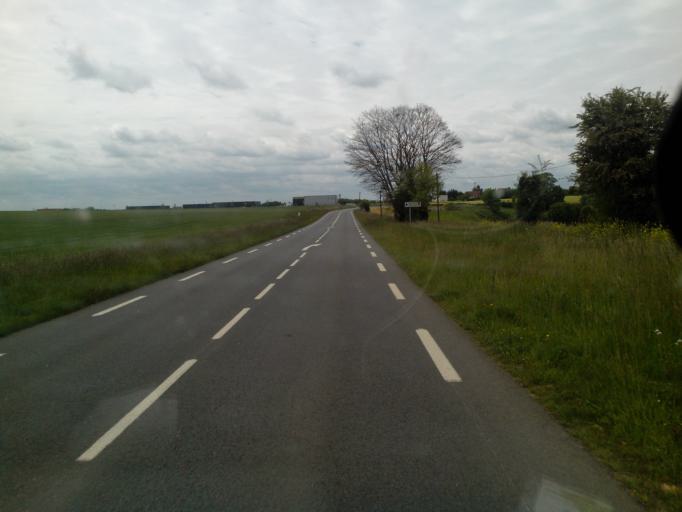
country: FR
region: Lower Normandy
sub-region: Departement du Calvados
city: Ranville
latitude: 49.2431
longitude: -0.2529
